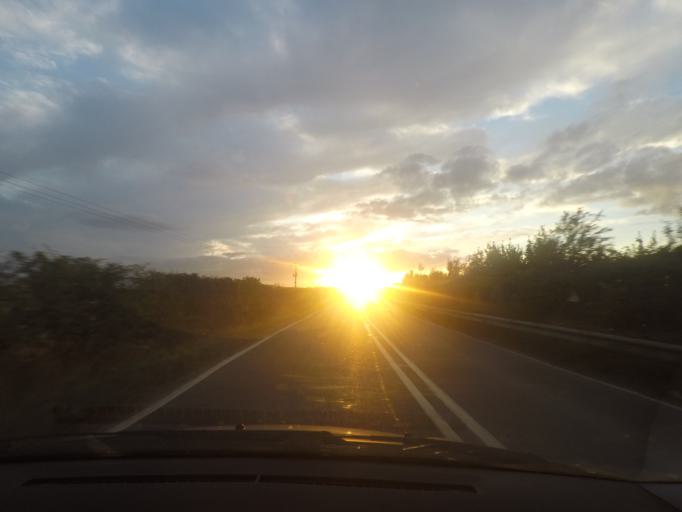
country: GB
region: England
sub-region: North Lincolnshire
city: Croxton
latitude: 53.5849
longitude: -0.3632
